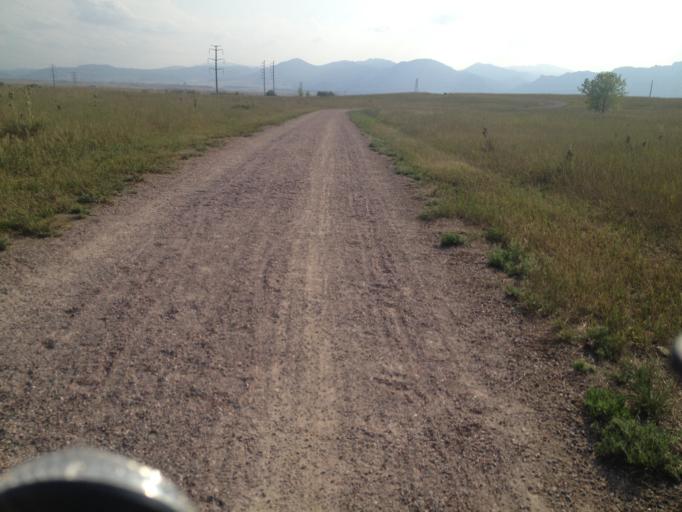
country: US
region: Colorado
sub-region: Boulder County
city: Superior
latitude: 39.9691
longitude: -105.1770
